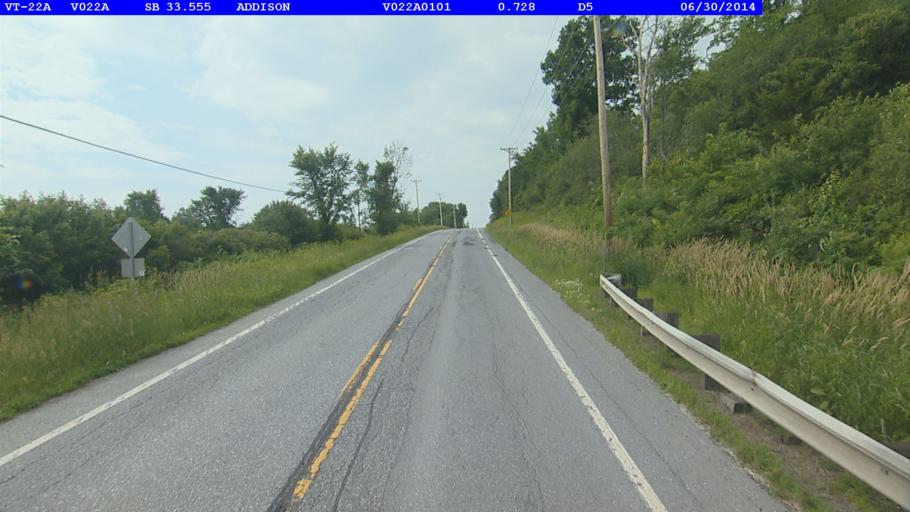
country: US
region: Vermont
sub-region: Addison County
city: Vergennes
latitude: 44.0404
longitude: -73.3056
